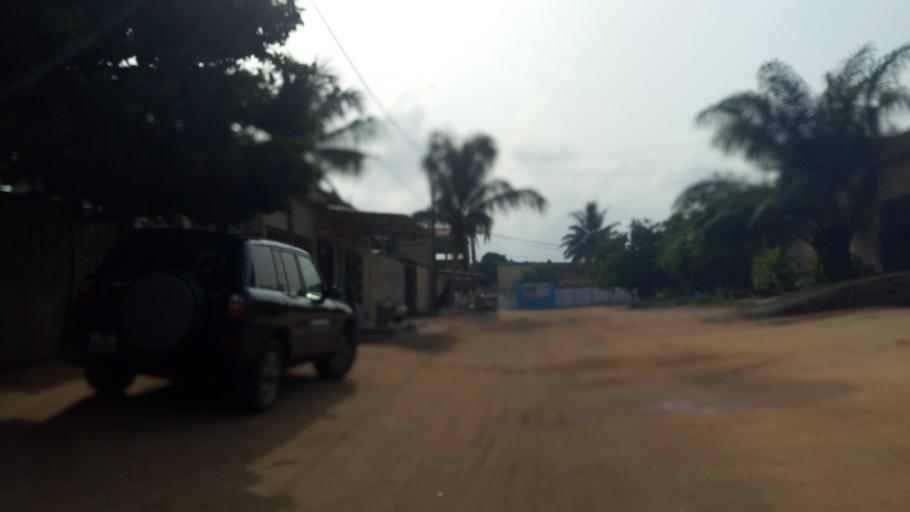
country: TG
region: Maritime
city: Lome
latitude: 6.1774
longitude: 1.1743
